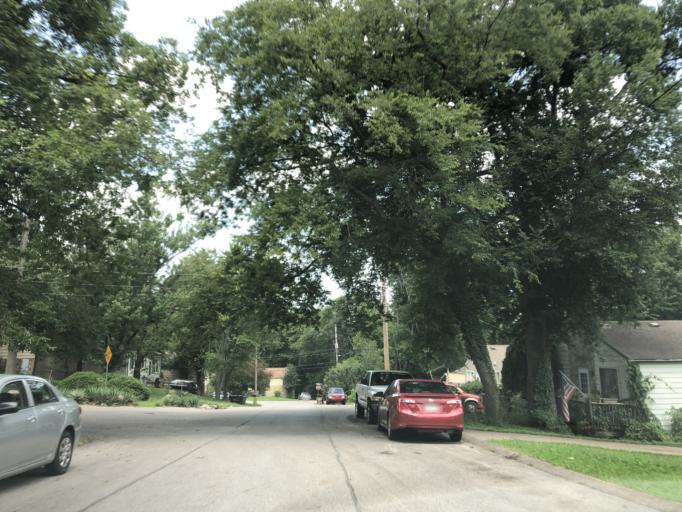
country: US
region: Tennessee
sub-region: Williamson County
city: Brentwood Estates
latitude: 36.0611
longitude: -86.6900
